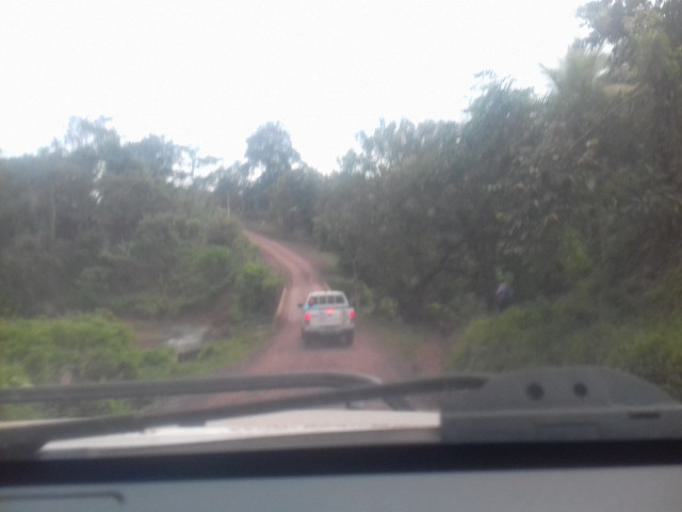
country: NI
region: Atlantico Norte (RAAN)
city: Waslala
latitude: 13.3946
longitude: -85.3252
